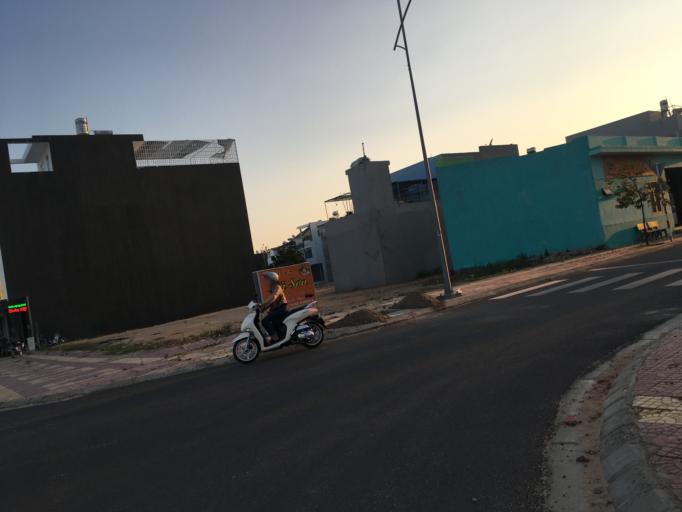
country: VN
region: Ninh Thuan
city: Phan Rang-Thap Cham
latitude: 11.5704
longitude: 108.9985
